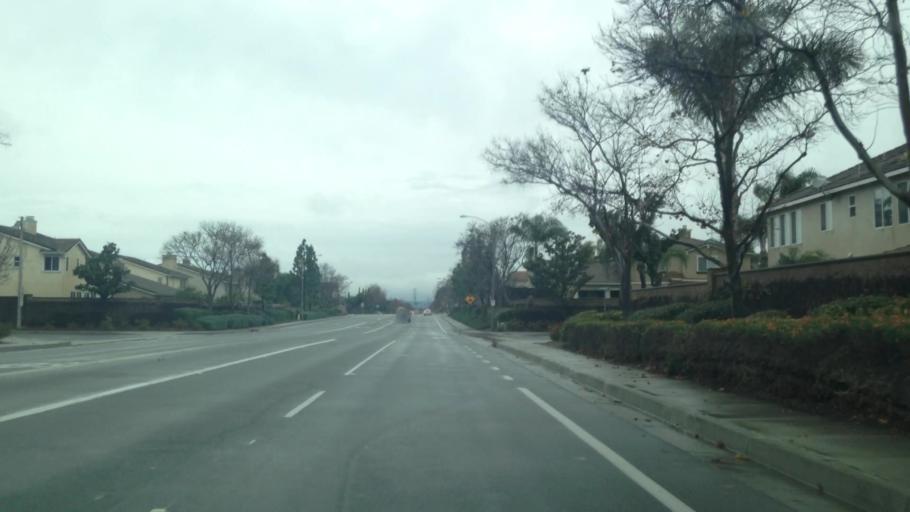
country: US
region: California
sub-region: Riverside County
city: Norco
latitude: 33.9682
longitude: -117.5774
